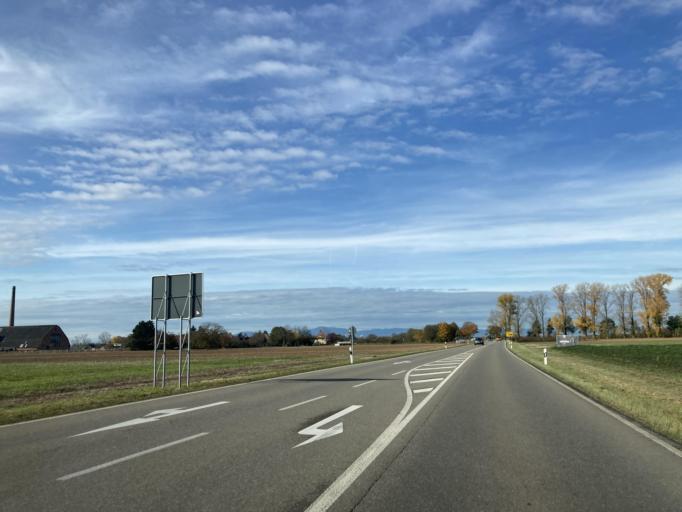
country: DE
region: Baden-Wuerttemberg
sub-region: Freiburg Region
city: Auggen
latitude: 47.8085
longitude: 7.5884
